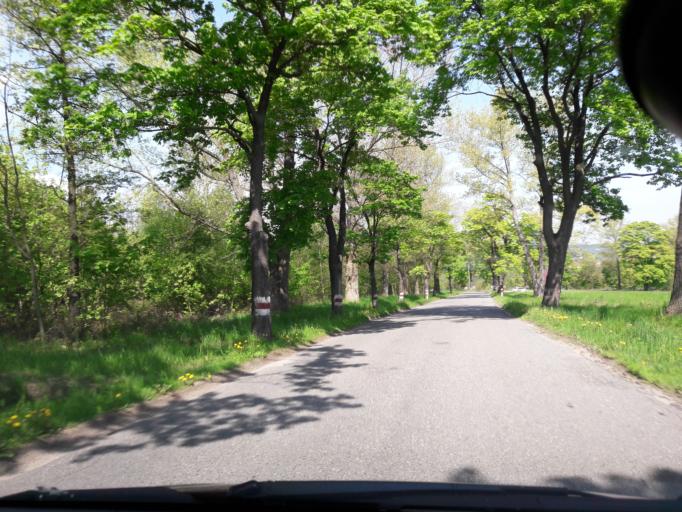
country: PL
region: Lower Silesian Voivodeship
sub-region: Powiat klodzki
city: Polanica-Zdroj
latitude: 50.3864
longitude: 16.5230
